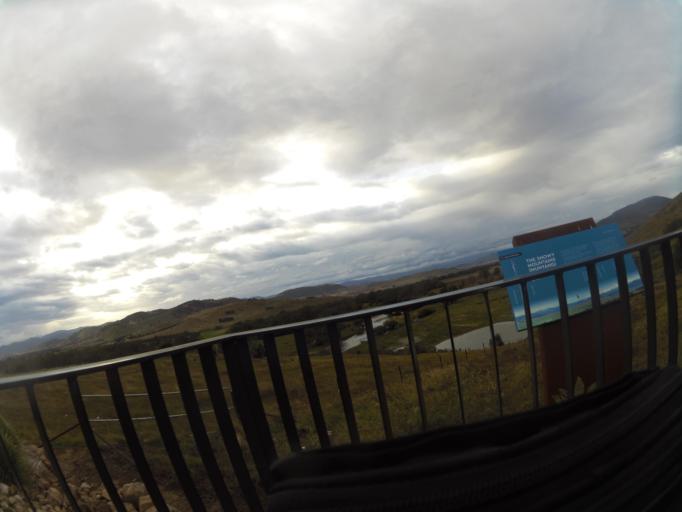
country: AU
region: New South Wales
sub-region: Snowy River
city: Jindabyne
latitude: -36.0853
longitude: 147.9786
